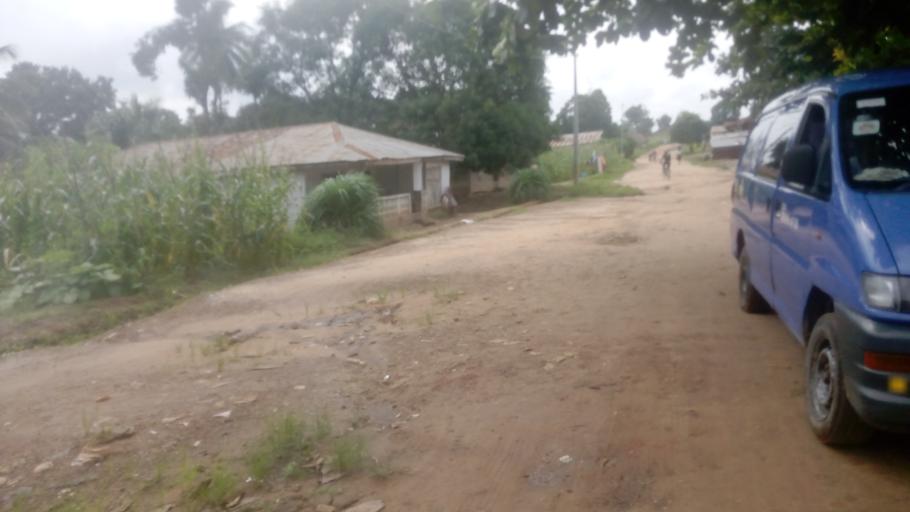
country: SL
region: Northern Province
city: Lunsar
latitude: 8.6916
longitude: -12.5372
